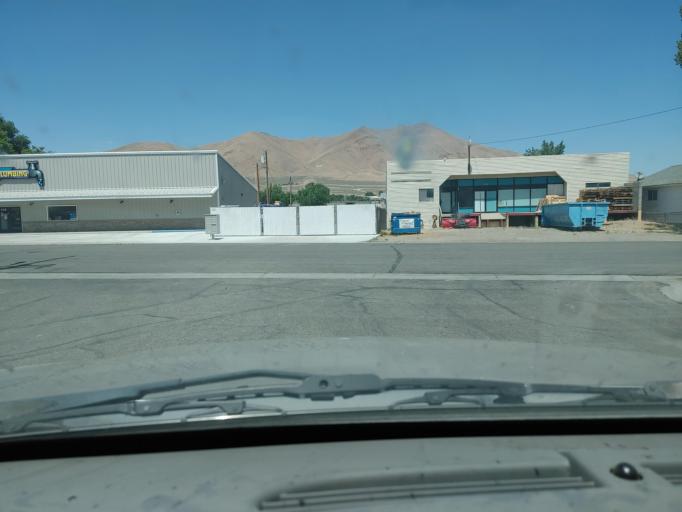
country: US
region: Nevada
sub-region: Humboldt County
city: Winnemucca
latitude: 40.9753
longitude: -117.7341
